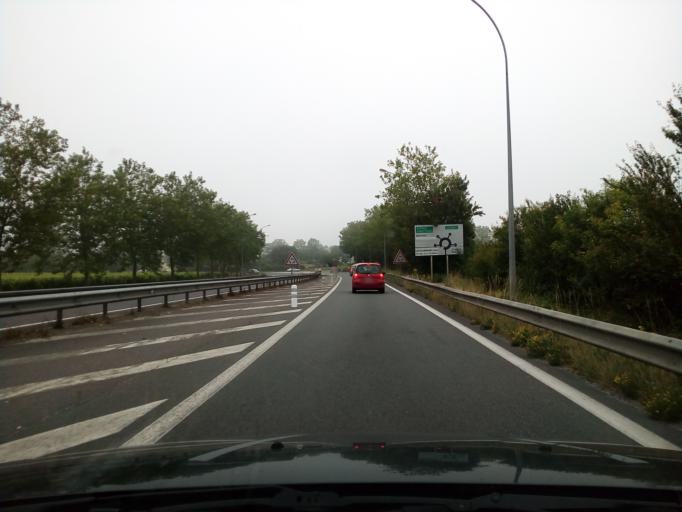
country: FR
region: Poitou-Charentes
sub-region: Departement de la Charente
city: Saint-Brice
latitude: 45.6810
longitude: -0.2898
